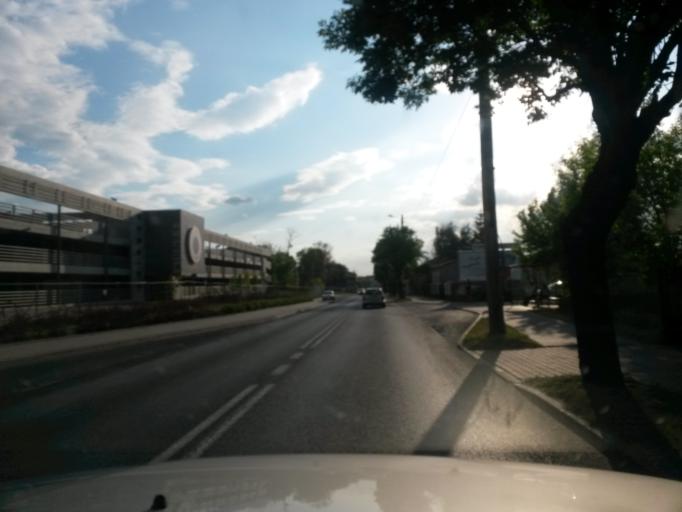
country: PL
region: Lodz Voivodeship
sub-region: Powiat belchatowski
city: Belchatow
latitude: 51.3706
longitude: 19.3736
